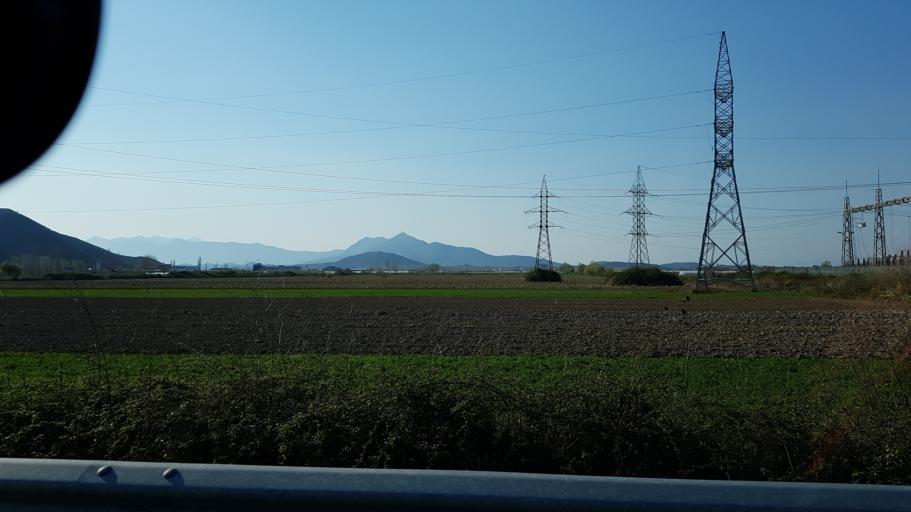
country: AL
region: Shkoder
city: Vukatane
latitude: 41.9865
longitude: 19.5478
